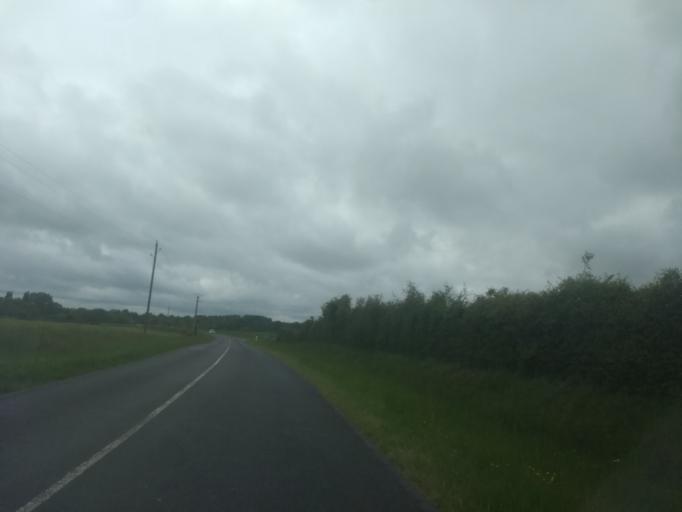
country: FR
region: Centre
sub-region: Departement d'Eure-et-Loir
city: La Loupe
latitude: 48.5083
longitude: 1.0410
